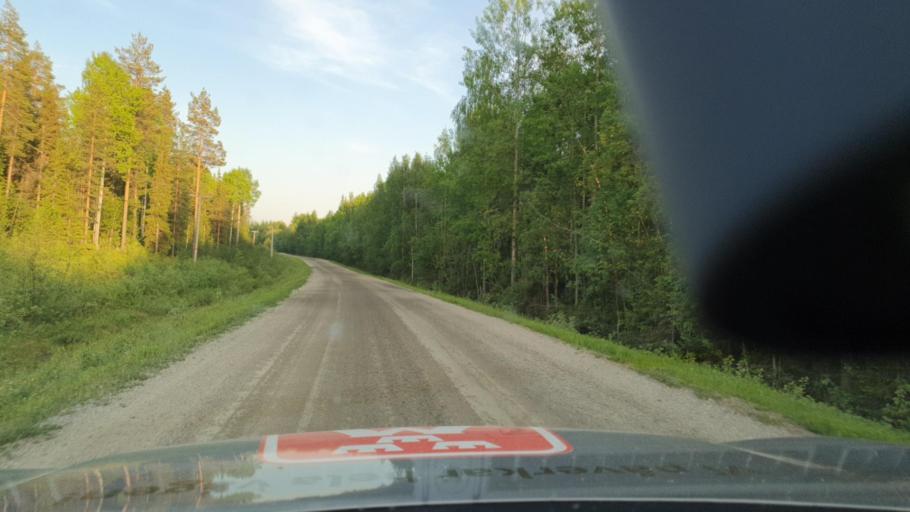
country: SE
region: Norrbotten
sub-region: Bodens Kommun
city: Boden
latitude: 66.1810
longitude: 21.5051
